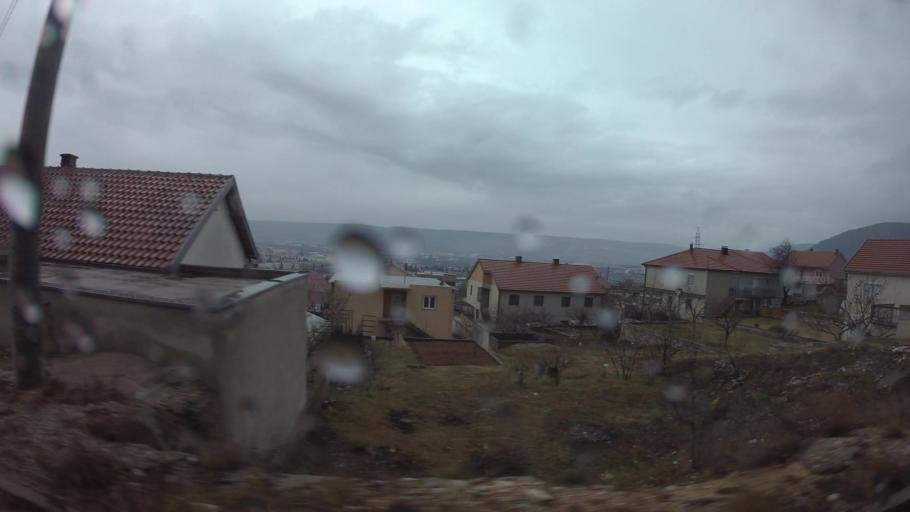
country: BA
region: Federation of Bosnia and Herzegovina
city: Rodoc
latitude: 43.3117
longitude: 17.8389
